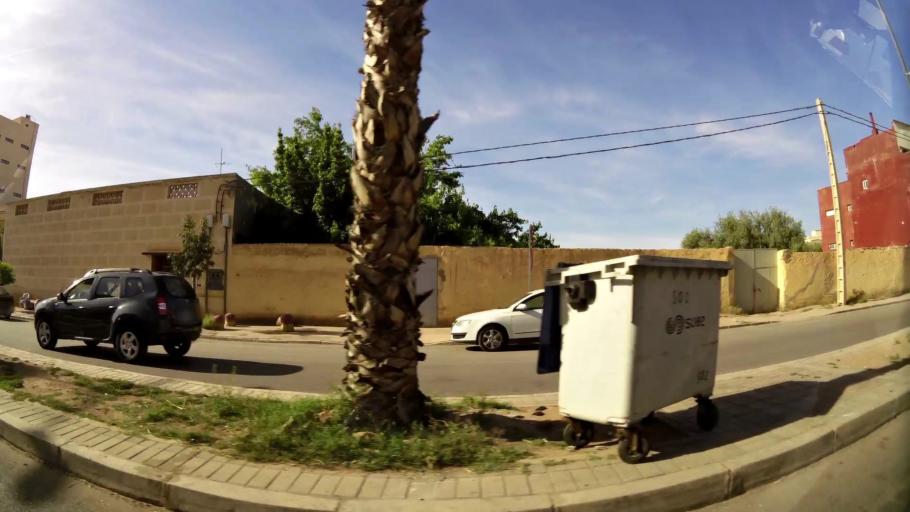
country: MA
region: Oriental
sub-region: Oujda-Angad
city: Oujda
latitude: 34.6681
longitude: -1.8987
